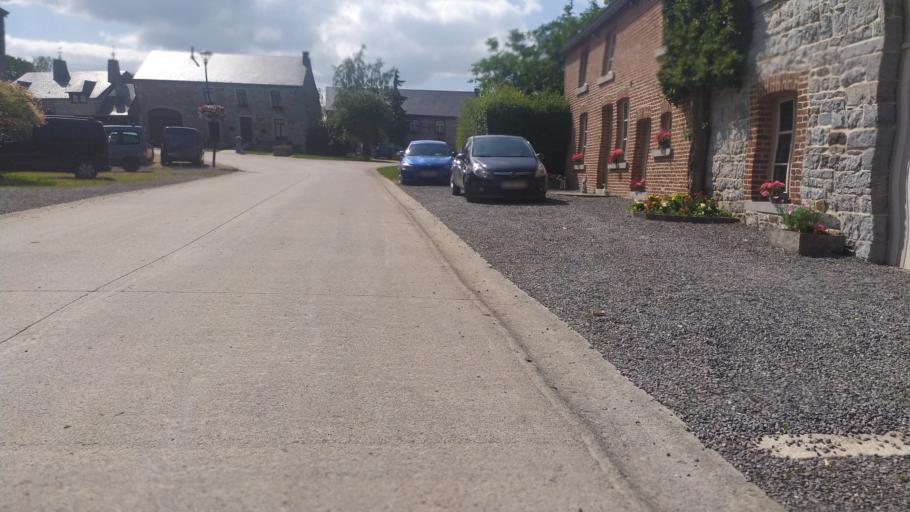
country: BE
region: Wallonia
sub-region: Province du Luxembourg
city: Wellin
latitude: 50.0683
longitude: 5.0683
